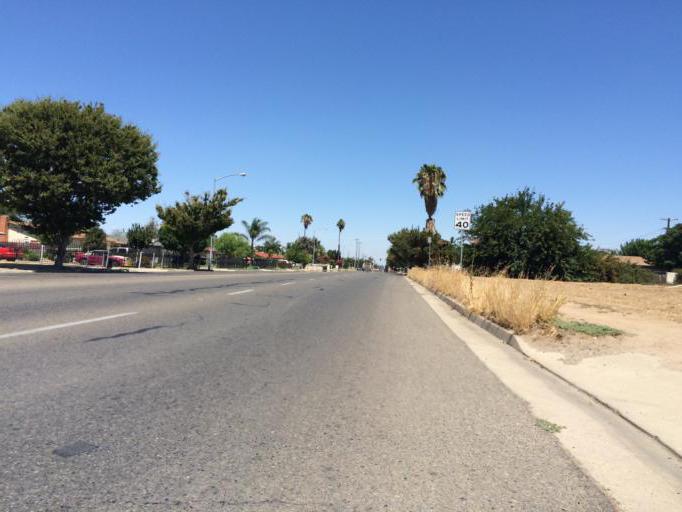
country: US
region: California
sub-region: Fresno County
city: Fresno
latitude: 36.7147
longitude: -119.7456
